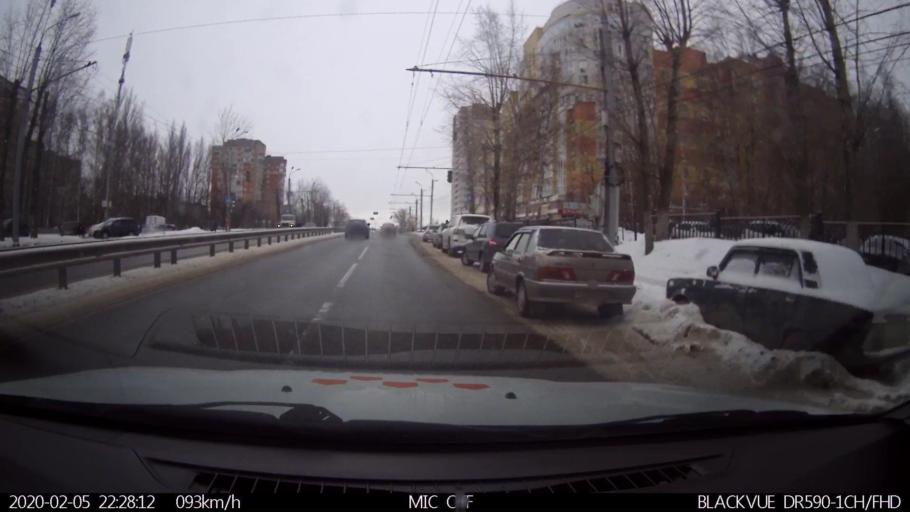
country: RU
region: Nizjnij Novgorod
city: Imeni Stepana Razina
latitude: 54.7592
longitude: 44.1286
